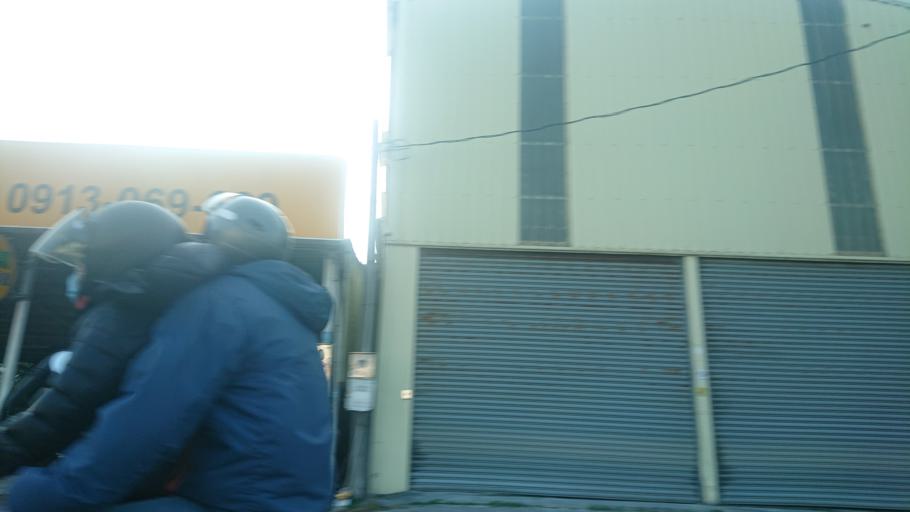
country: TW
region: Taiwan
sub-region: Tainan
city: Tainan
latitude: 23.0731
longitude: 120.2142
